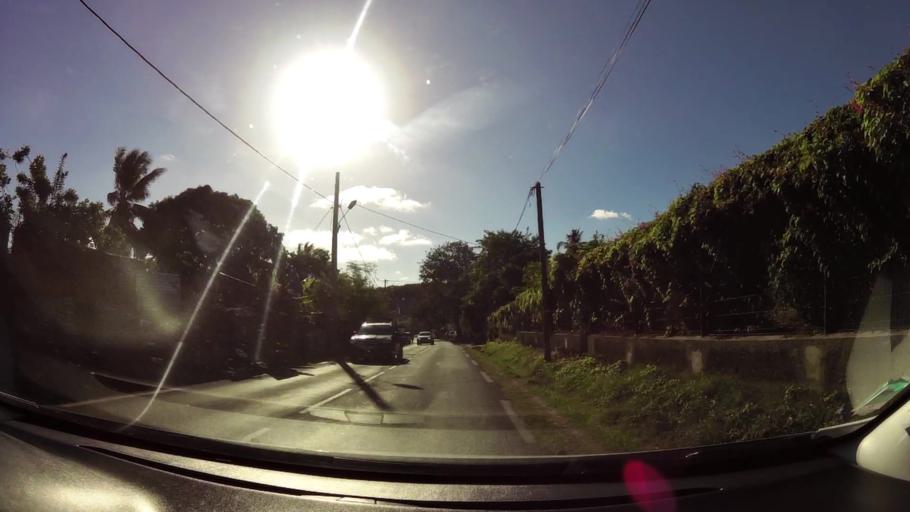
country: YT
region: Pamandzi
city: Pamandzi
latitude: -12.7934
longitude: 45.2717
